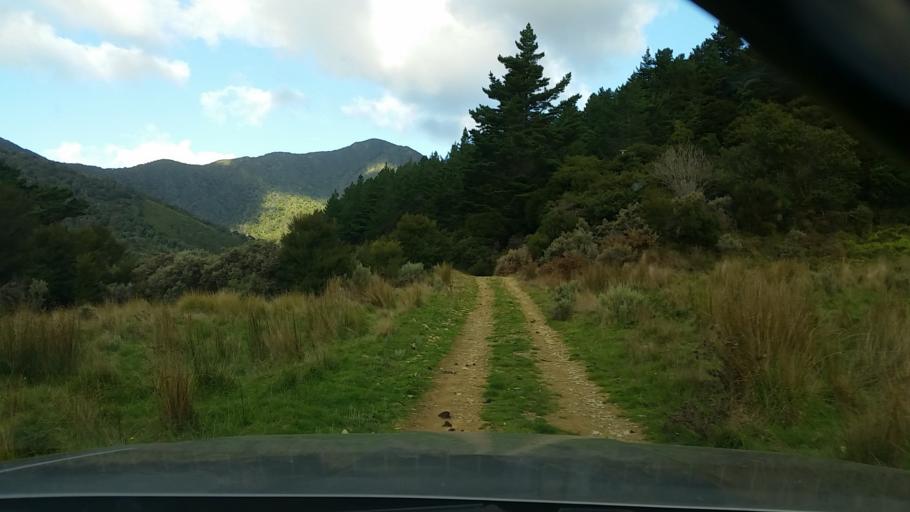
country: NZ
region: Marlborough
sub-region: Marlborough District
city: Picton
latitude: -41.0612
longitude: 174.1162
